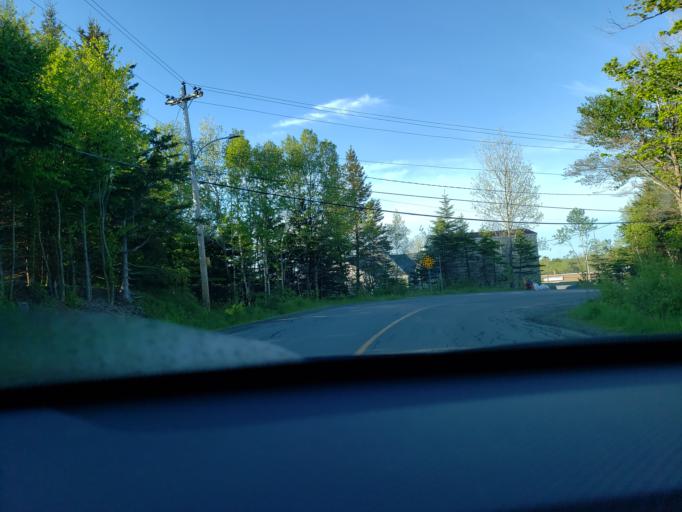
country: CA
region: Nova Scotia
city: Cole Harbour
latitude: 44.7401
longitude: -63.3809
